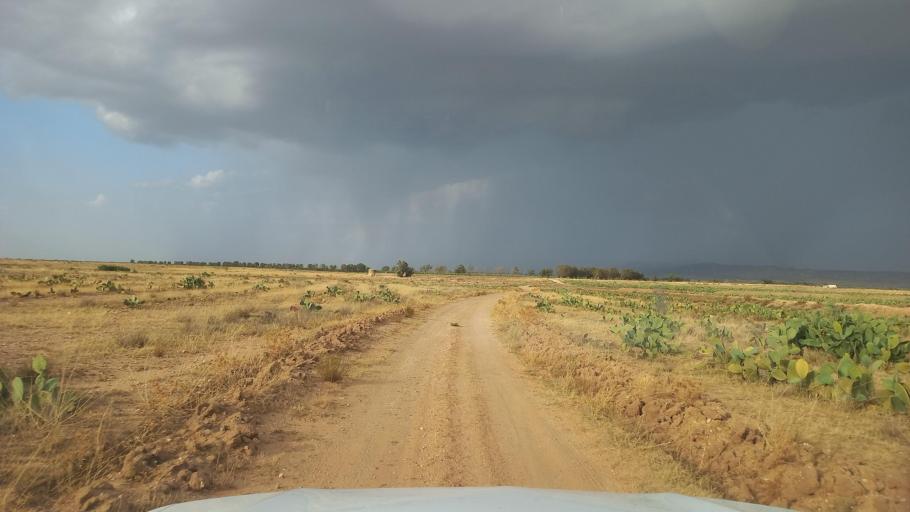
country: TN
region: Al Qasrayn
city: Kasserine
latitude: 35.2890
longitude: 9.0459
